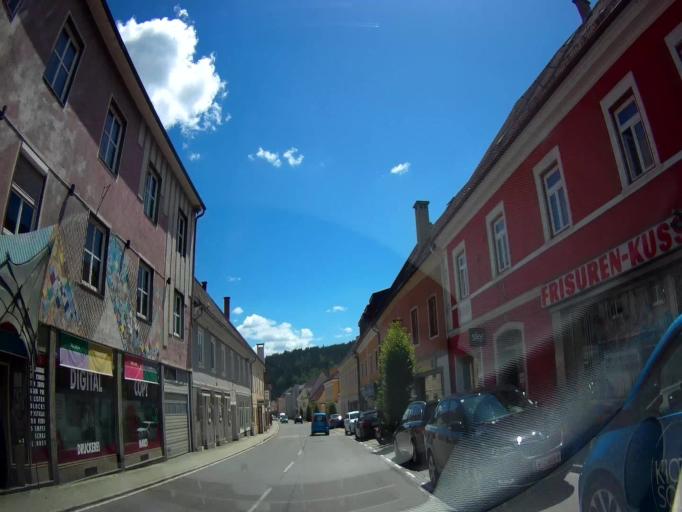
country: AT
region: Carinthia
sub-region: Politischer Bezirk Sankt Veit an der Glan
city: Sankt Veit an der Glan
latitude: 46.7661
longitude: 14.3602
